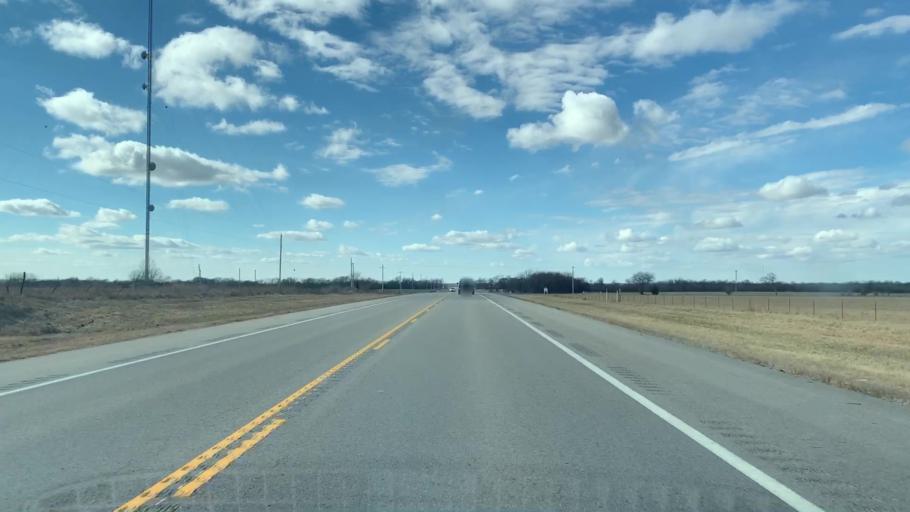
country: US
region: Kansas
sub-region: Labette County
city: Oswego
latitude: 37.3402
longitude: -95.0281
